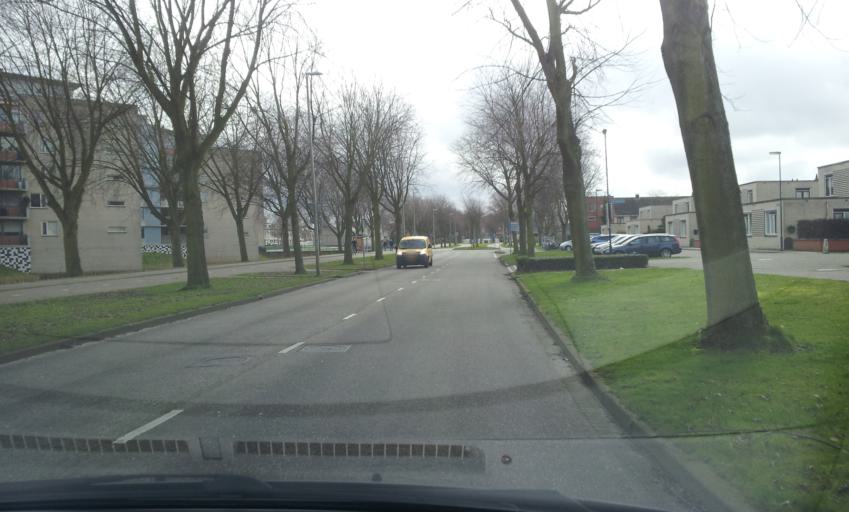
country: NL
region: South Holland
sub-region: Gemeente Zoetermeer
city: Zoetermeer
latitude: 52.0430
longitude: 4.4736
